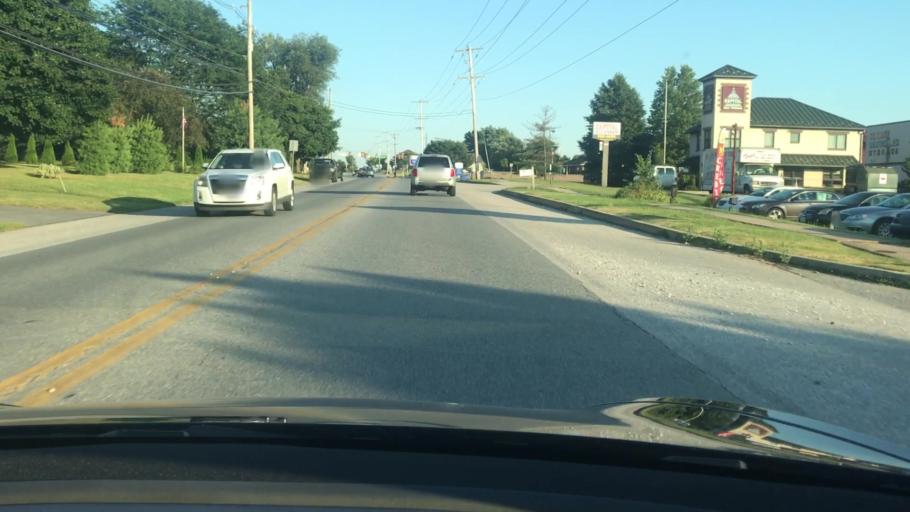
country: US
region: Pennsylvania
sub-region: York County
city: Dover
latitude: 39.9951
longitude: -76.8441
